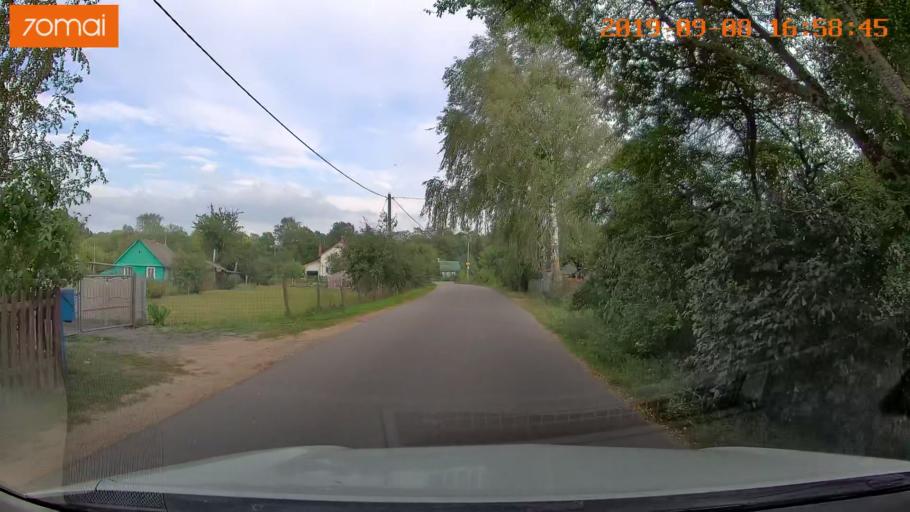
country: BY
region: Grodnenskaya
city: Hrodna
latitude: 53.7252
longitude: 23.9306
